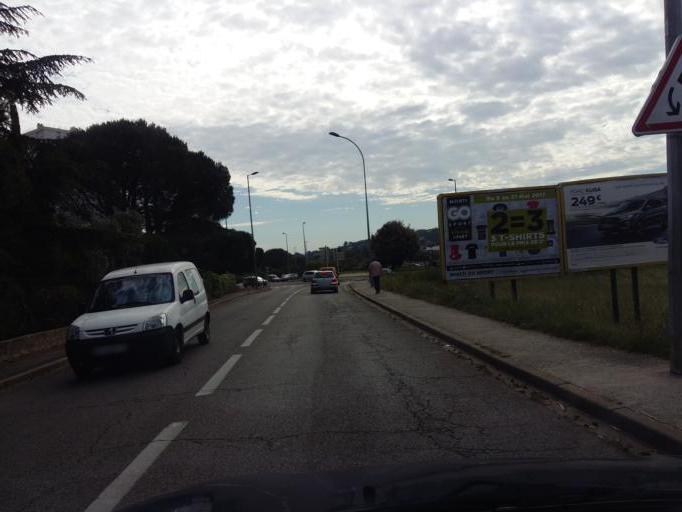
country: FR
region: Languedoc-Roussillon
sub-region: Departement du Gard
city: Bagnols-sur-Ceze
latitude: 44.1550
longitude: 4.6154
